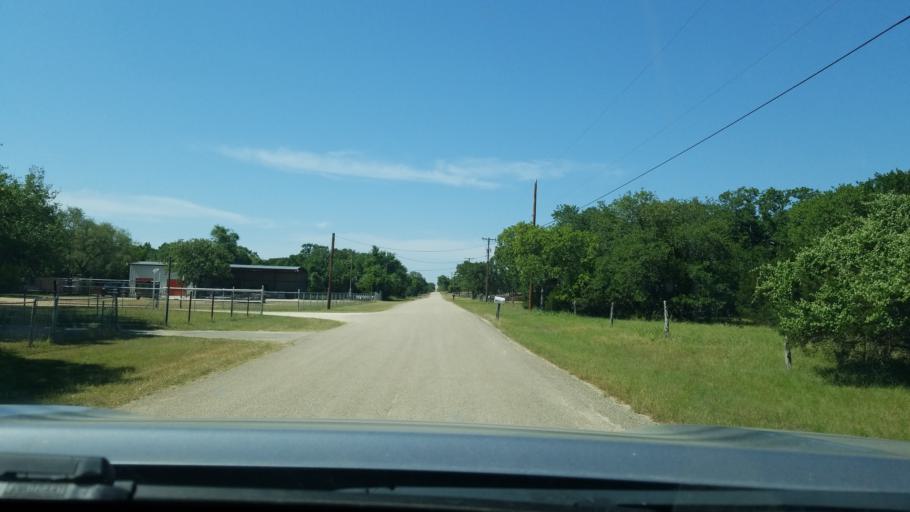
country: US
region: Texas
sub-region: Bexar County
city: Timberwood Park
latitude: 29.7509
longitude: -98.5153
